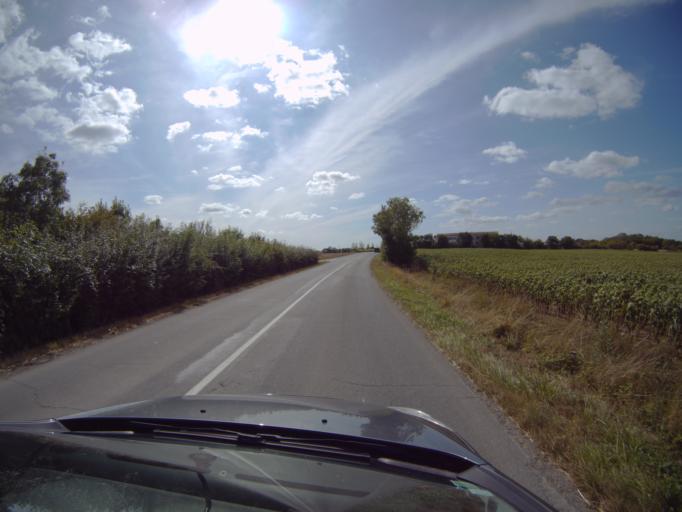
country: FR
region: Poitou-Charentes
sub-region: Departement des Deux-Sevres
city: Saint-Hilaire-la-Palud
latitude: 46.2593
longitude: -0.7025
